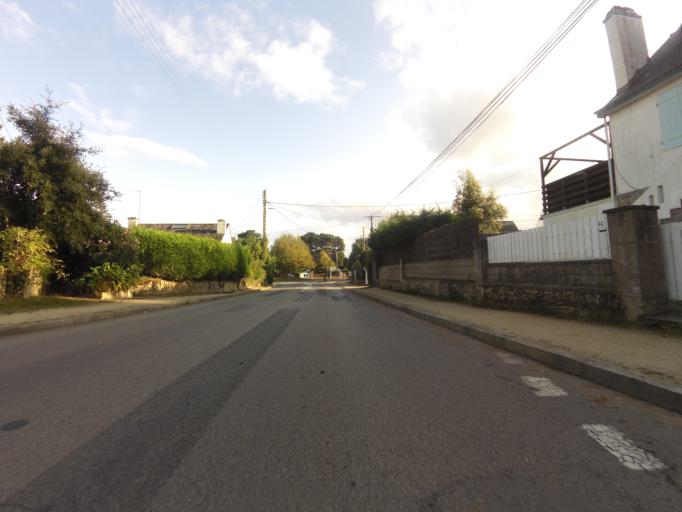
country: FR
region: Brittany
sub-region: Departement du Morbihan
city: Carnac
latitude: 47.5782
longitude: -3.0751
